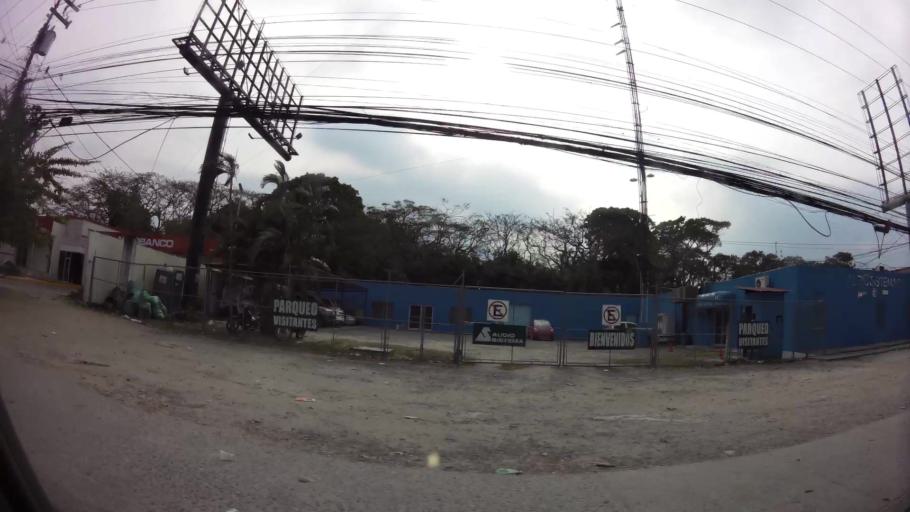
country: HN
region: Cortes
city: San Pedro Sula
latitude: 15.5193
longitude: -88.0254
